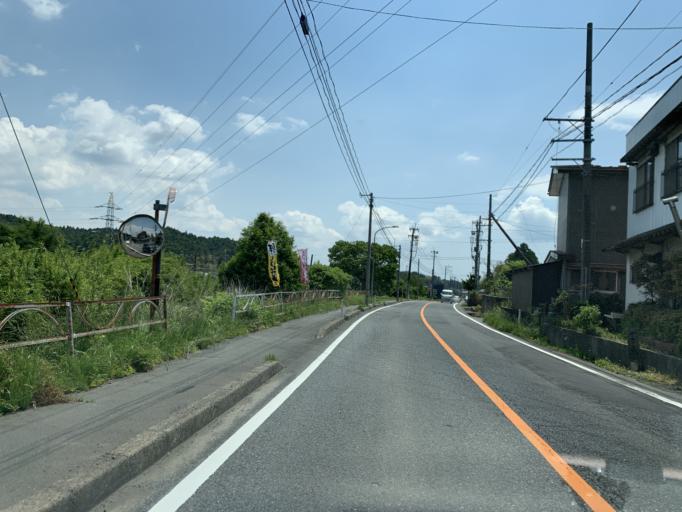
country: JP
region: Miyagi
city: Wakuya
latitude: 38.4878
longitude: 141.0917
